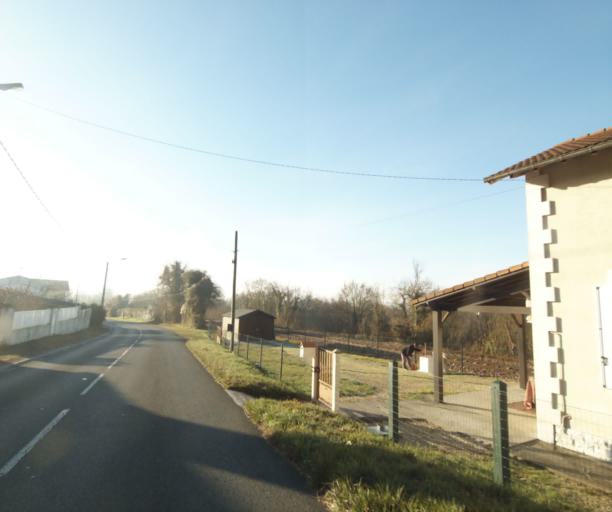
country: FR
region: Poitou-Charentes
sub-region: Departement de la Charente-Maritime
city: Saintes
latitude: 45.7649
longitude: -0.6184
